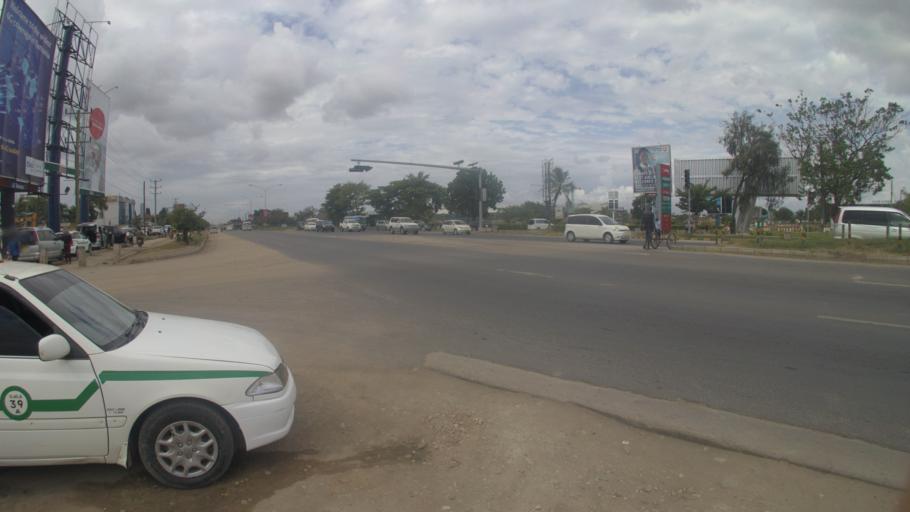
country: TZ
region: Dar es Salaam
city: Dar es Salaam
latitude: -6.8632
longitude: 39.2059
